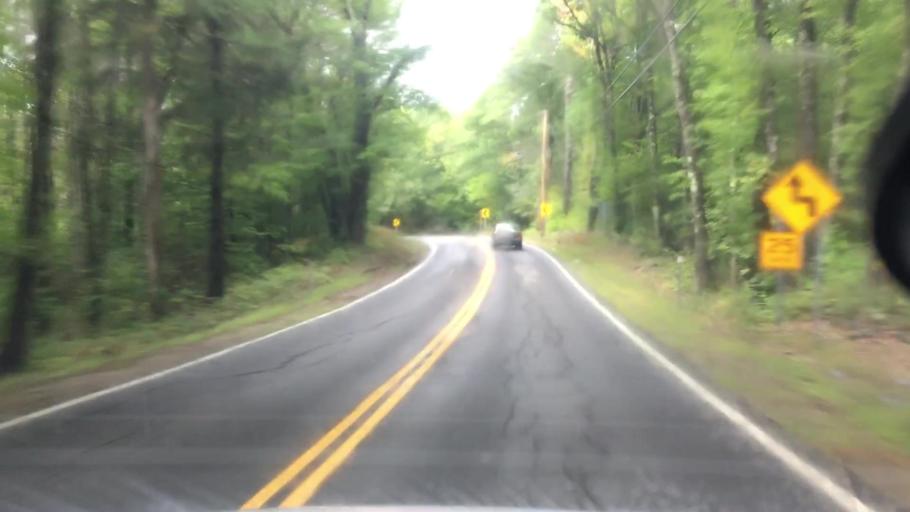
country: US
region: Maine
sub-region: York County
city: Parsonsfield
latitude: 43.6683
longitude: -70.9906
